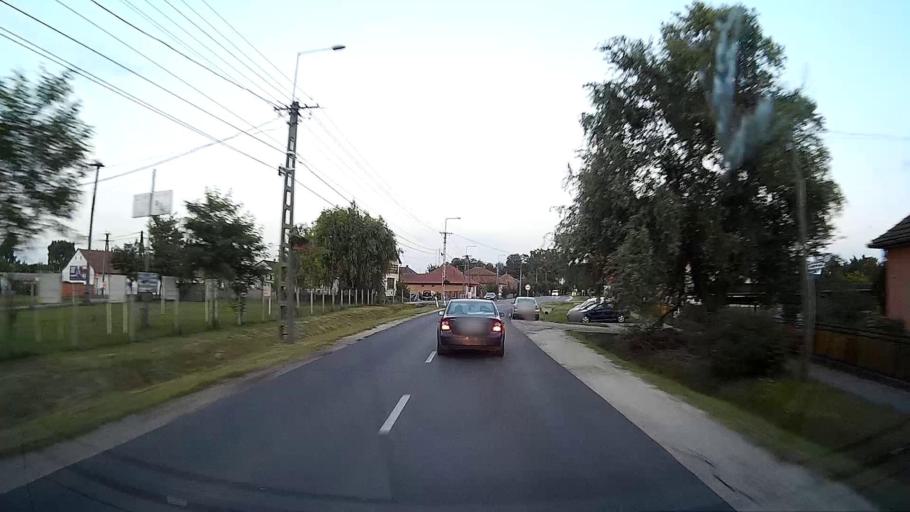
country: HU
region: Pest
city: Albertirsa
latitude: 47.2534
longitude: 19.6030
